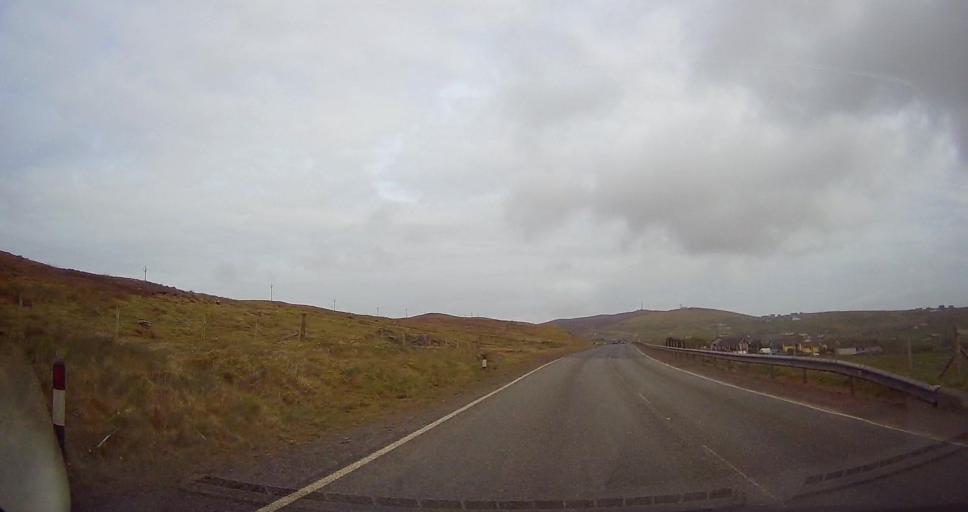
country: GB
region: Scotland
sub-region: Shetland Islands
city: Lerwick
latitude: 60.1241
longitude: -1.2171
